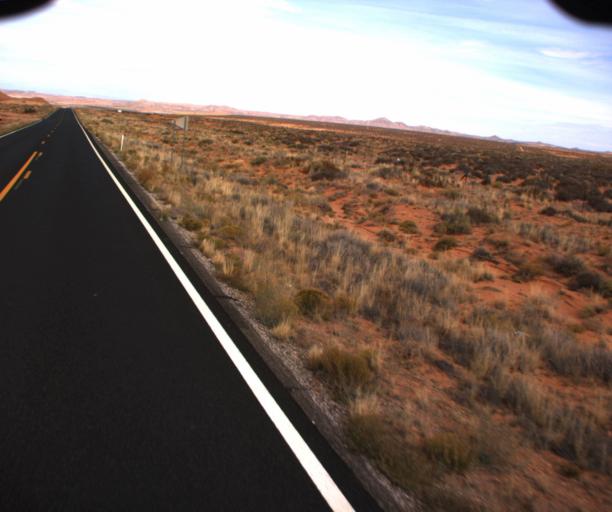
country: US
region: Arizona
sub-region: Apache County
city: Many Farms
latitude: 36.8860
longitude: -109.6278
